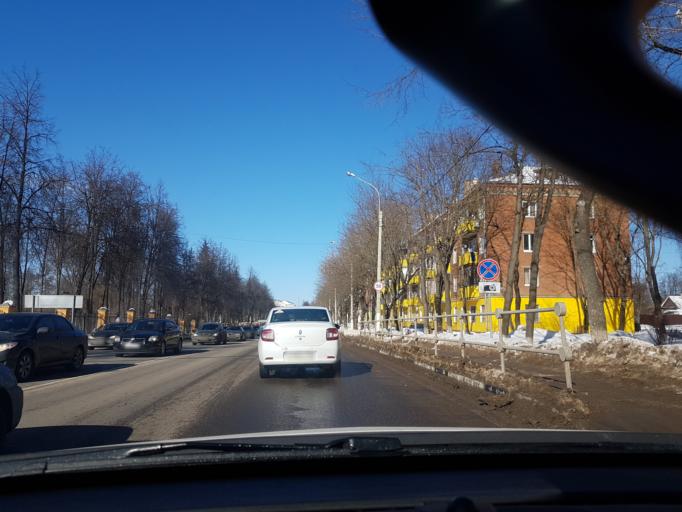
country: RU
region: Moskovskaya
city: Istra
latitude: 55.9166
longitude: 36.8583
